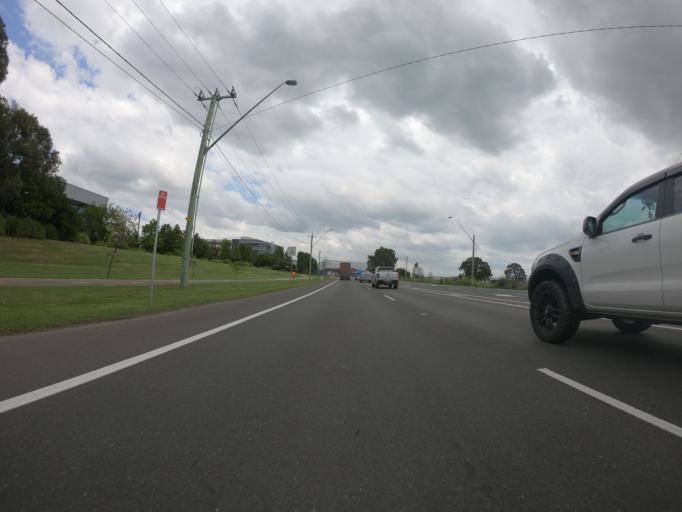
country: AU
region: New South Wales
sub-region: Blacktown
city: Mount Druitt
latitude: -33.8184
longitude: 150.7761
